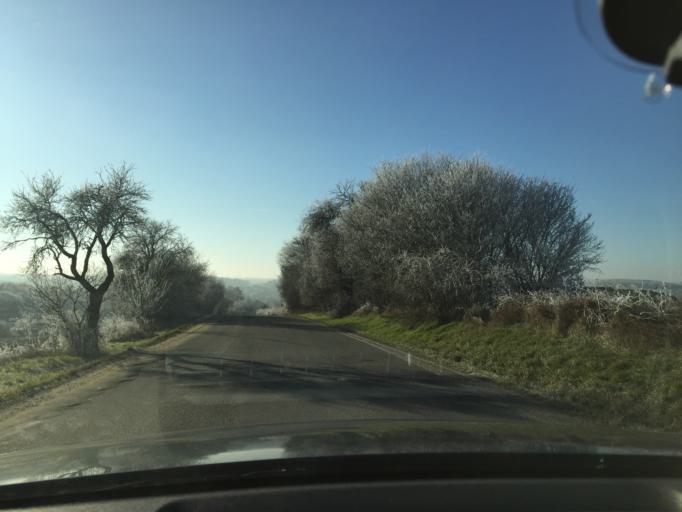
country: CZ
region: Central Bohemia
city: Trebotov
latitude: 50.0040
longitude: 14.2737
